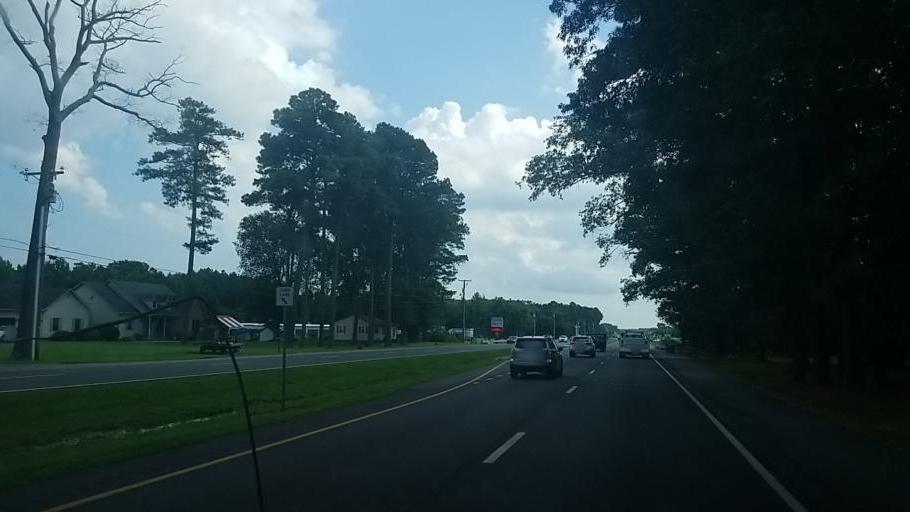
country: US
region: Delaware
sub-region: Sussex County
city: Selbyville
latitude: 38.4704
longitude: -75.2346
